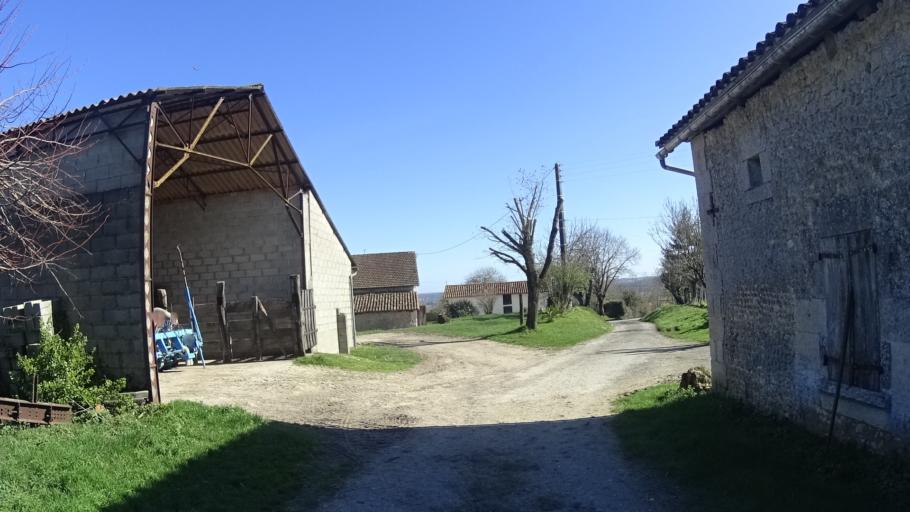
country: FR
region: Aquitaine
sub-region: Departement de la Dordogne
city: Saint-Aulaye
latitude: 45.2442
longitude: 0.1350
